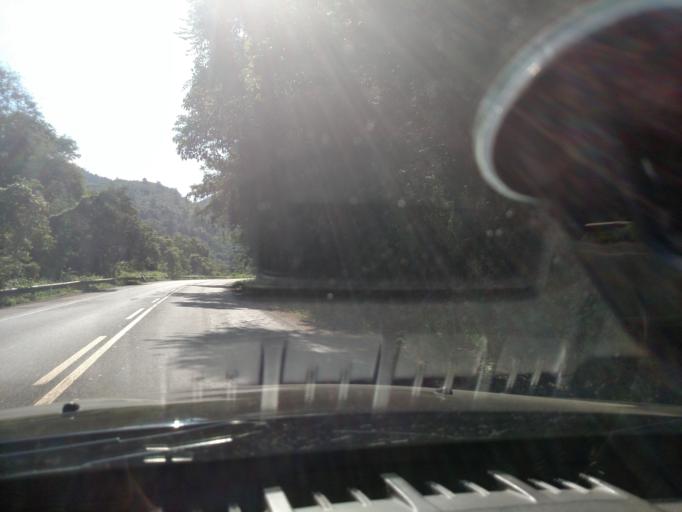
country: BR
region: Santa Catarina
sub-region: Ibirama
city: Ibirama
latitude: -27.0871
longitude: -49.4755
